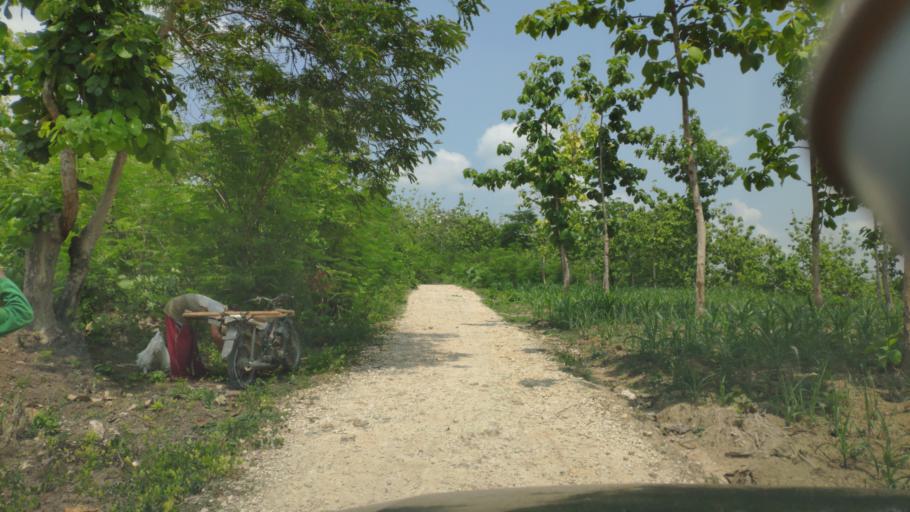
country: ID
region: Central Java
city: Palon
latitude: -7.0221
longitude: 111.4958
